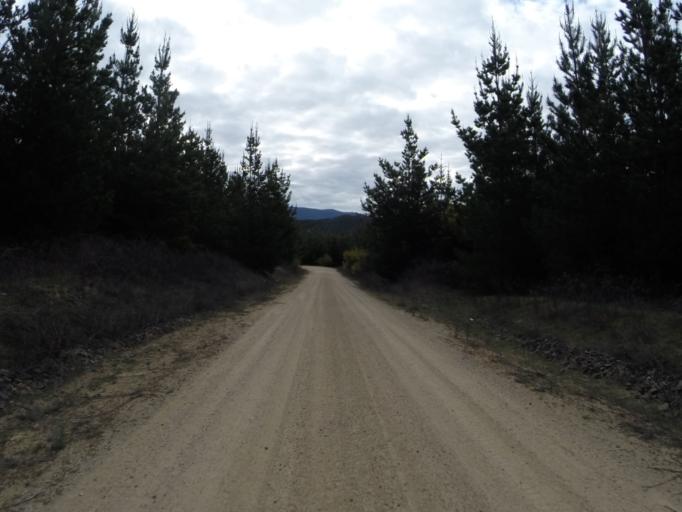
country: AU
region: Australian Capital Territory
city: Macquarie
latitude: -35.3438
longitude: 148.9344
